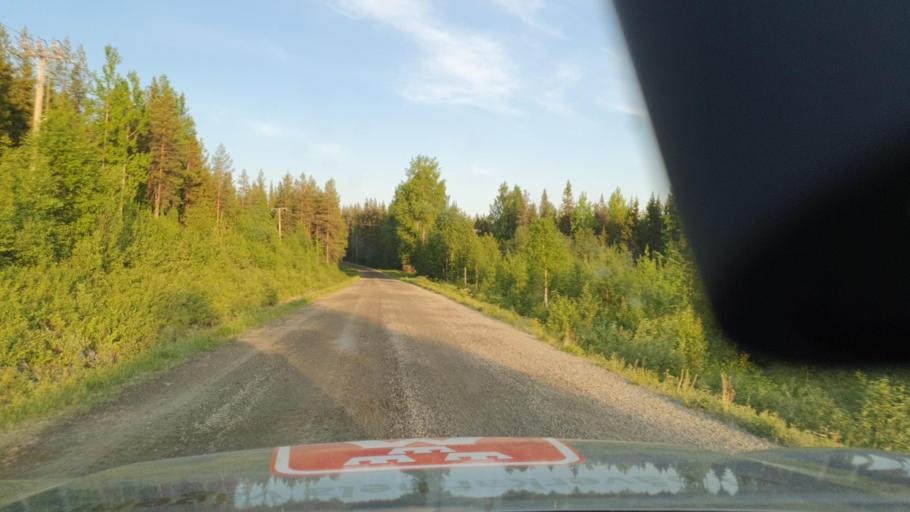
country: SE
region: Norrbotten
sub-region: Bodens Kommun
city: Boden
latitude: 66.1101
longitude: 21.5657
